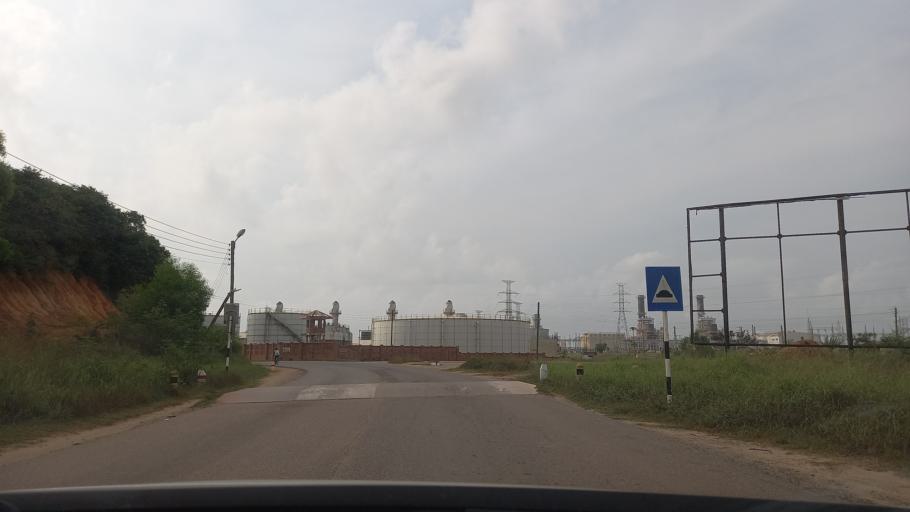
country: GH
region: Western
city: Shama Junction
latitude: 4.9771
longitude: -1.6588
